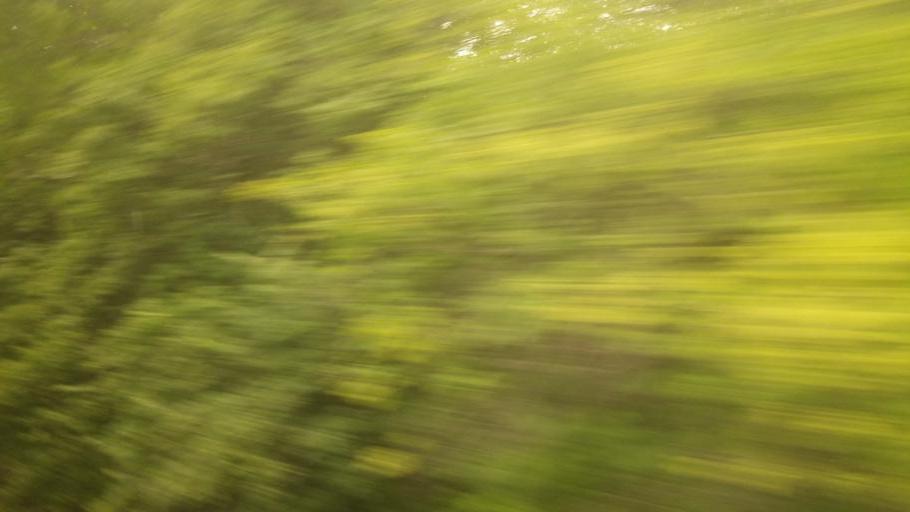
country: US
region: Kansas
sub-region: Shawnee County
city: Topeka
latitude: 39.0288
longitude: -95.6738
